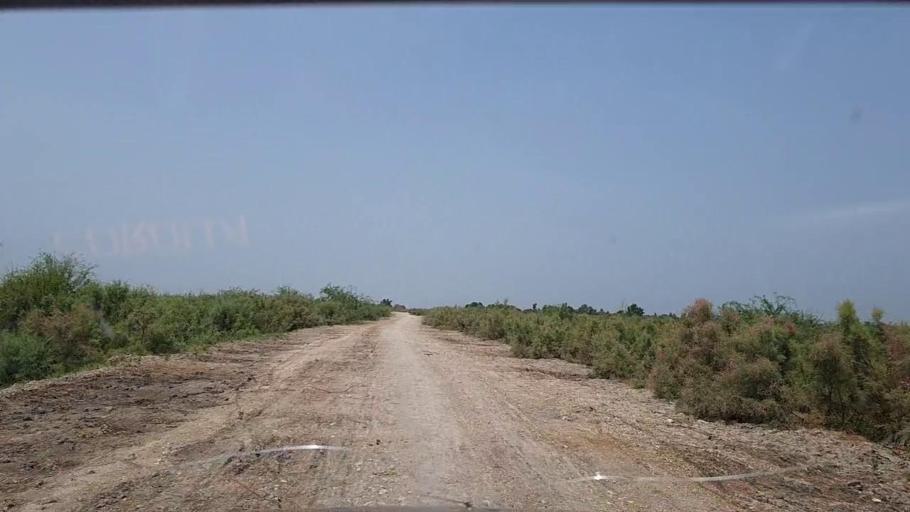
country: PK
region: Sindh
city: Adilpur
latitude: 27.8988
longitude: 69.2357
